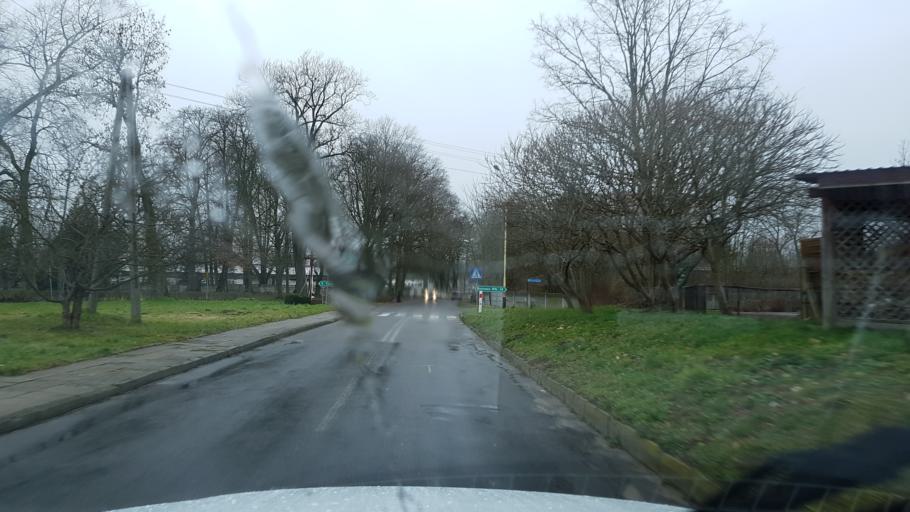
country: PL
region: West Pomeranian Voivodeship
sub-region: Powiat lobeski
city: Dobra
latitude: 53.5819
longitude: 15.3179
